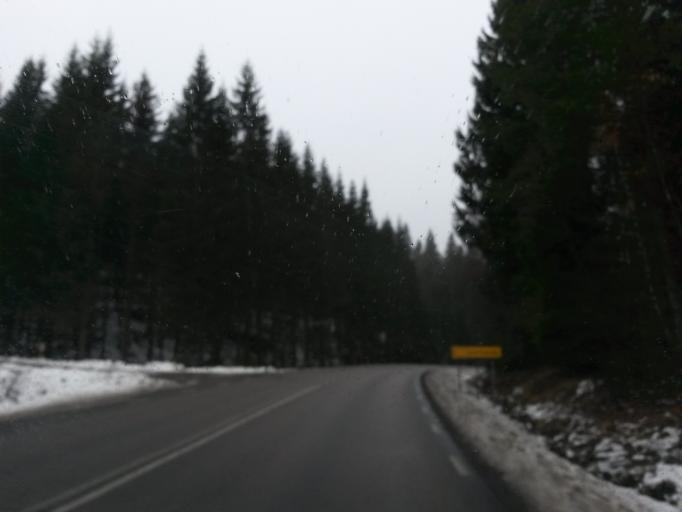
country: SE
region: Vaestra Goetaland
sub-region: Tranemo Kommun
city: Langhem
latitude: 57.6980
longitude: 13.2896
